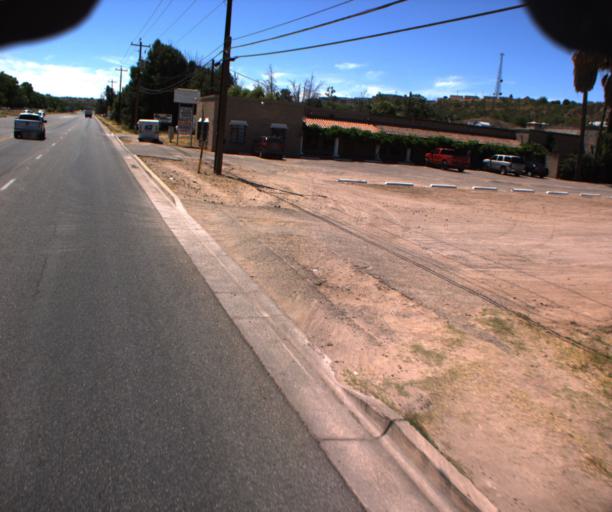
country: US
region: Arizona
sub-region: Santa Cruz County
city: Nogales
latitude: 31.3782
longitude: -110.9406
